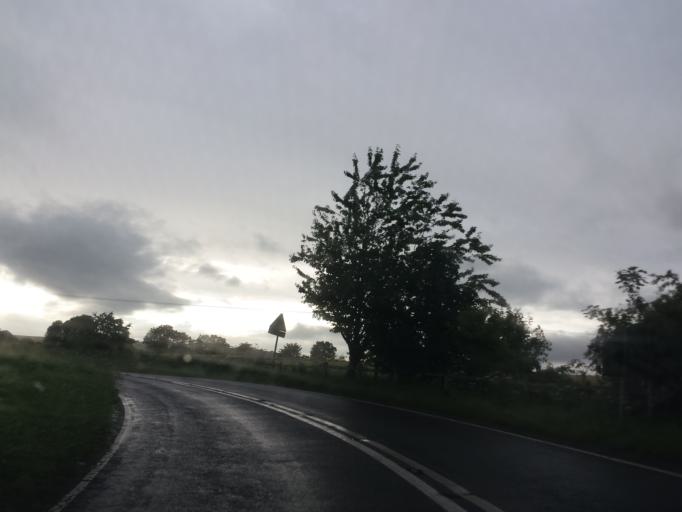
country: GB
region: Scotland
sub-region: Fife
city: Cupar
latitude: 56.3357
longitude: -3.0497
